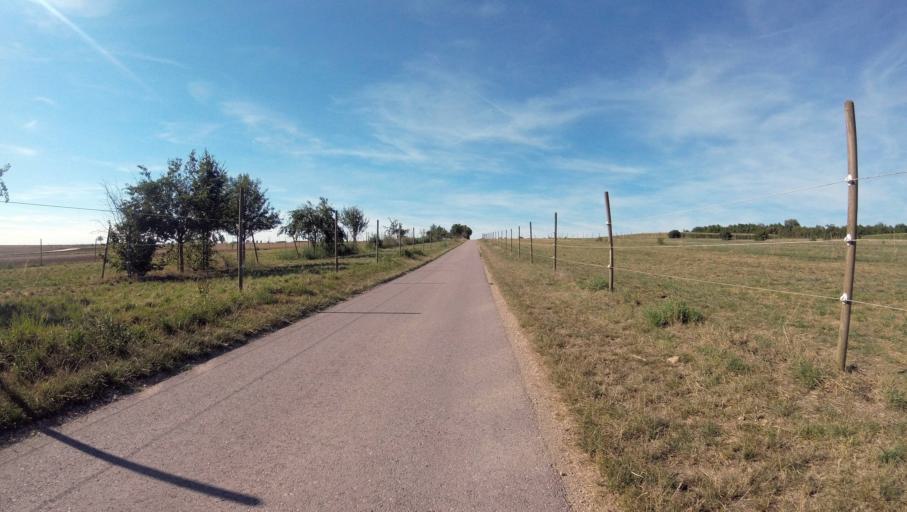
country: DE
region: Baden-Wuerttemberg
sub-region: Regierungsbezirk Stuttgart
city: Kirchberg an der Murr
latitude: 48.9501
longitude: 9.3461
